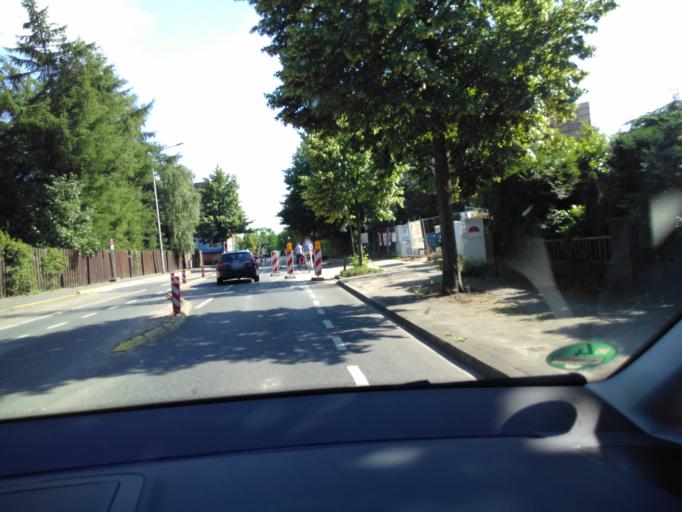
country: DE
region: North Rhine-Westphalia
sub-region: Regierungsbezirk Dusseldorf
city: Hilden
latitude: 51.1511
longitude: 6.9403
